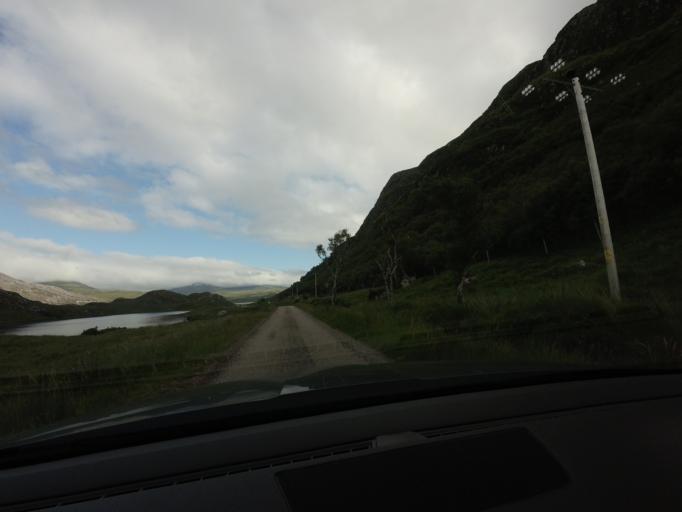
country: GB
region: Scotland
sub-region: Highland
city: Ullapool
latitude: 58.3437
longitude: -4.9536
